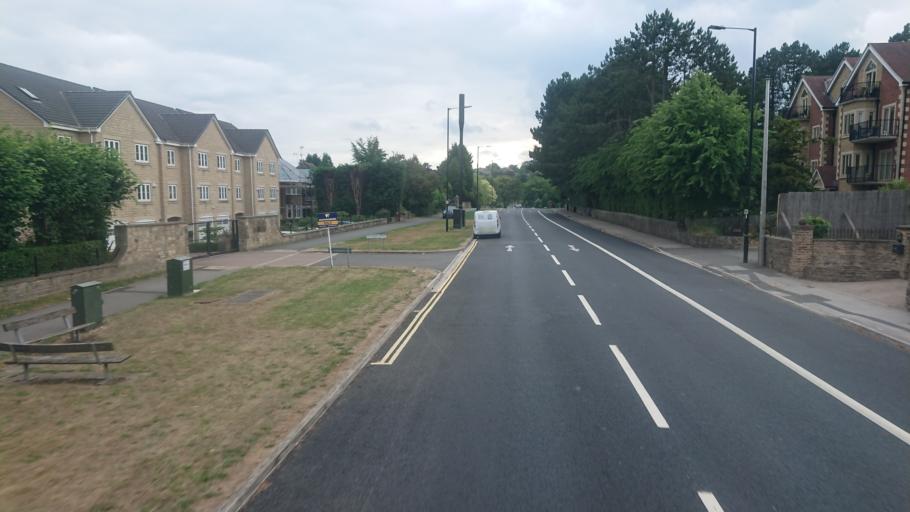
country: GB
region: England
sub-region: Sheffield
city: Sheffield
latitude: 53.3534
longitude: -1.5154
